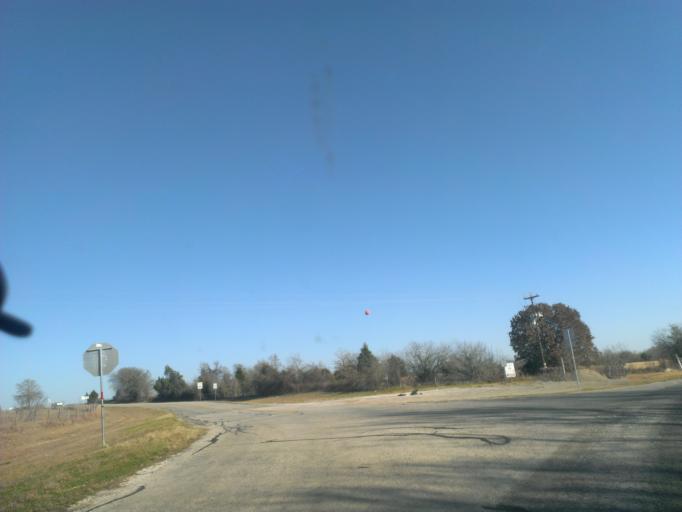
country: US
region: Texas
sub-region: Bastrop County
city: Elgin
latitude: 30.4417
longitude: -97.2610
